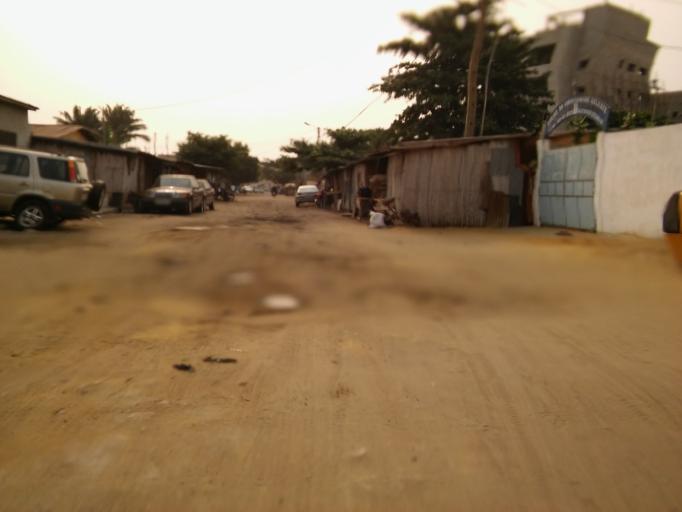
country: BJ
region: Littoral
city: Cotonou
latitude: 6.3596
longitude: 2.4031
